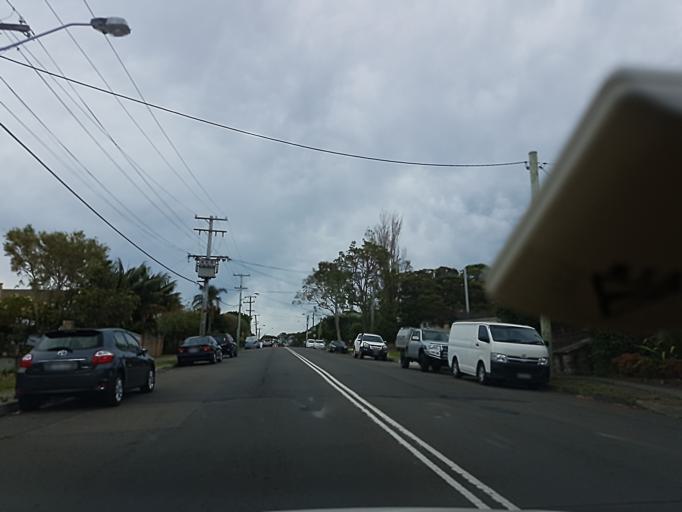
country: AU
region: New South Wales
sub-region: Warringah
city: Brookvale
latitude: -33.7568
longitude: 151.2647
